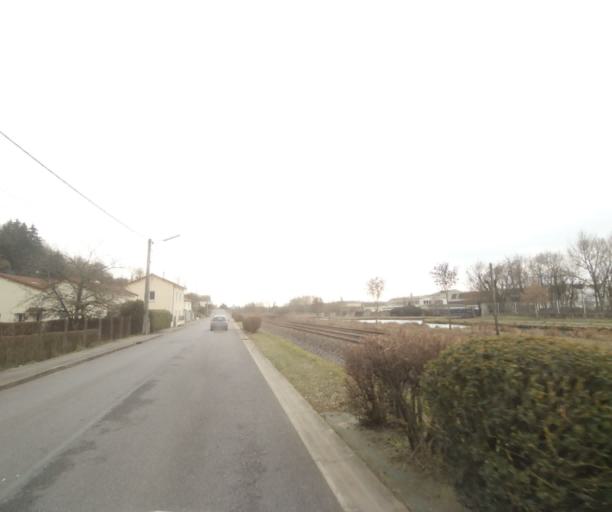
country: FR
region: Lorraine
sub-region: Departement de la Meuse
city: Ancerville
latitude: 48.6252
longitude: 4.9971
